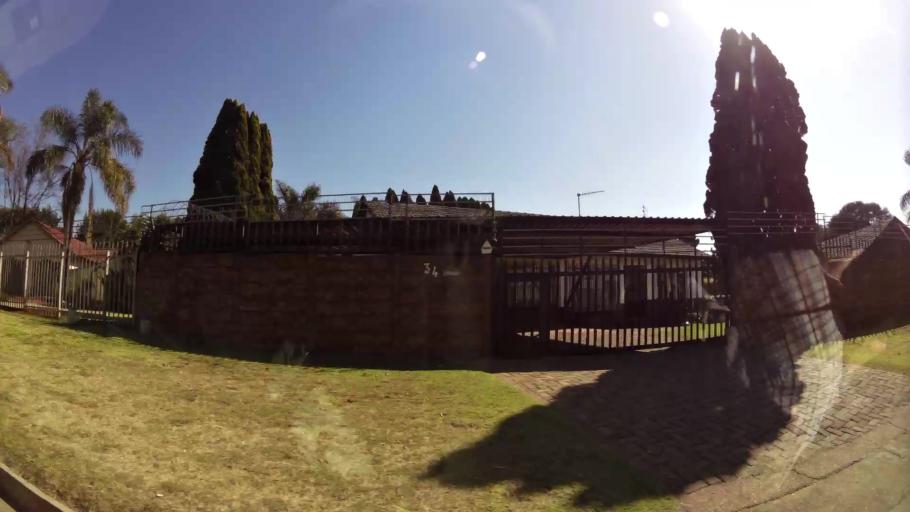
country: ZA
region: Gauteng
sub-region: City of Johannesburg Metropolitan Municipality
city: Modderfontein
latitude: -26.0575
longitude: 28.2086
